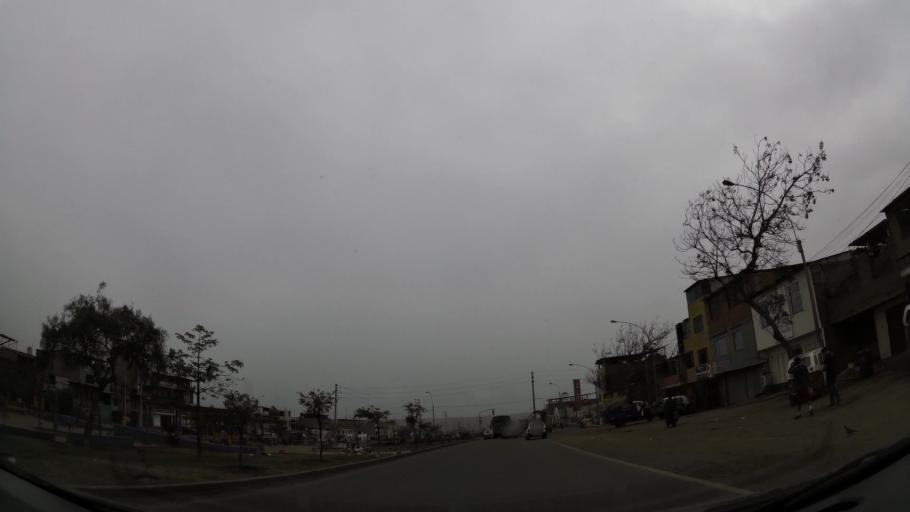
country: PE
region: Lima
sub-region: Lima
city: Surco
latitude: -12.2204
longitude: -76.9317
